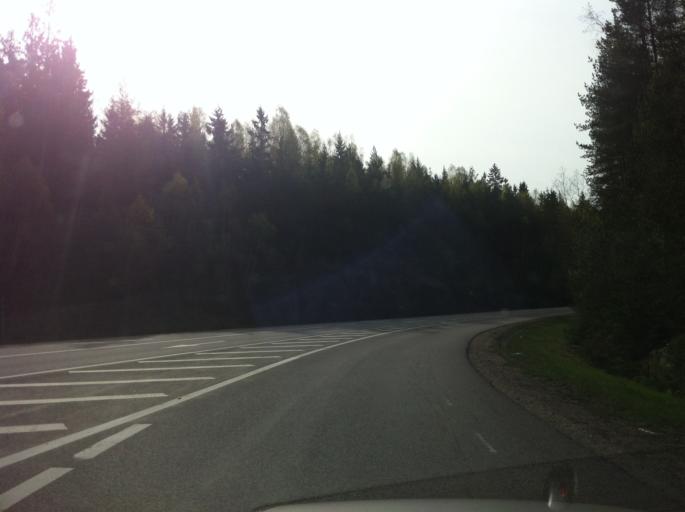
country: SE
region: Vaestra Goetaland
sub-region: Bollebygds Kommun
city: Bollebygd
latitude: 57.6717
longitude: 12.6012
